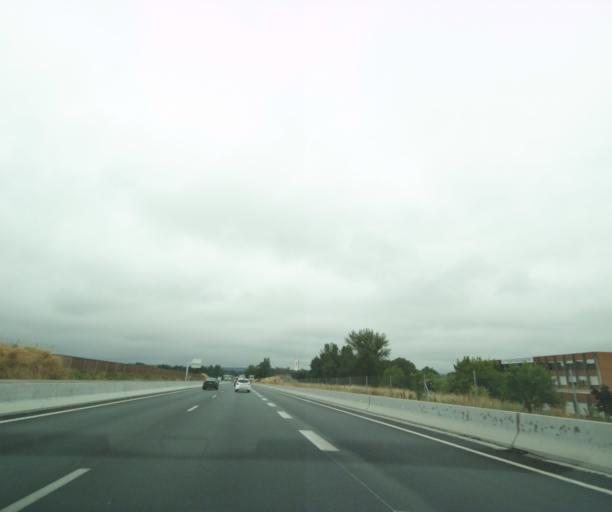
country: FR
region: Midi-Pyrenees
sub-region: Departement du Tarn
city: Albi
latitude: 43.9225
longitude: 2.1693
